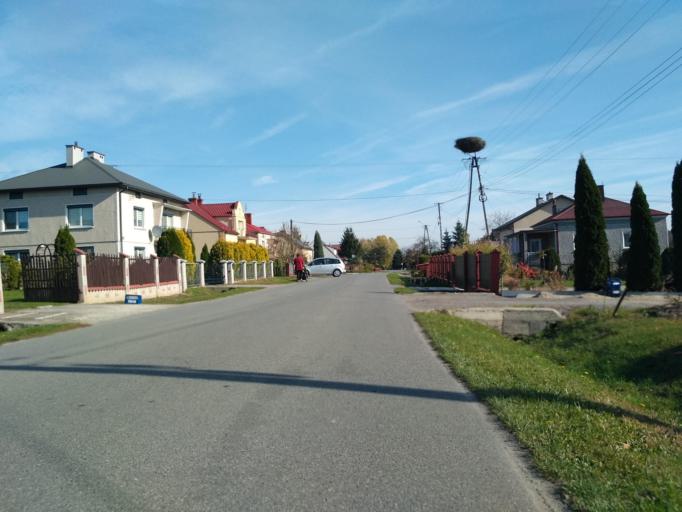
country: PL
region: Subcarpathian Voivodeship
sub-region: Powiat rzeszowski
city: Trzciana
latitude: 50.0776
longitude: 21.8008
